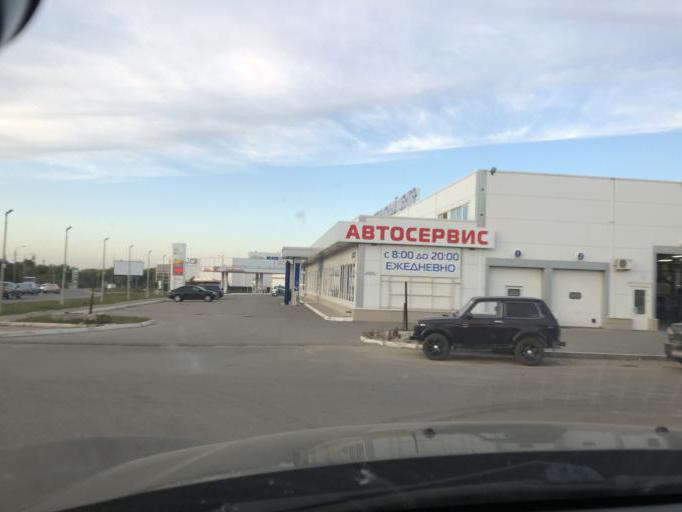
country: RU
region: Tula
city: Tula
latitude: 54.1656
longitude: 37.6411
